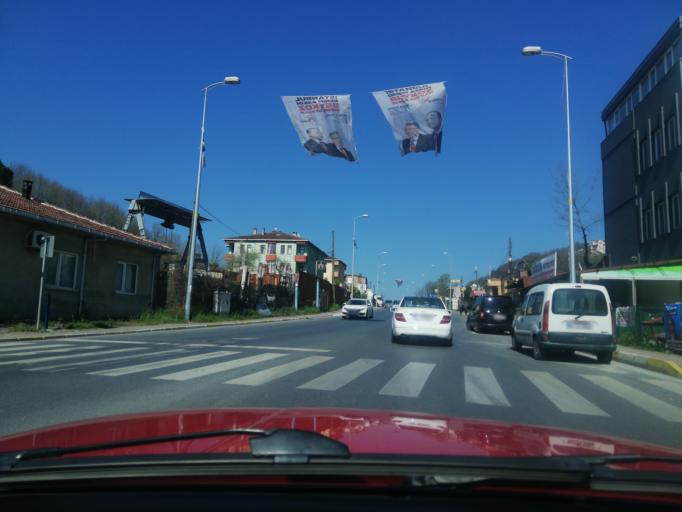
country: TR
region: Istanbul
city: Umraniye
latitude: 41.0865
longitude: 29.1362
